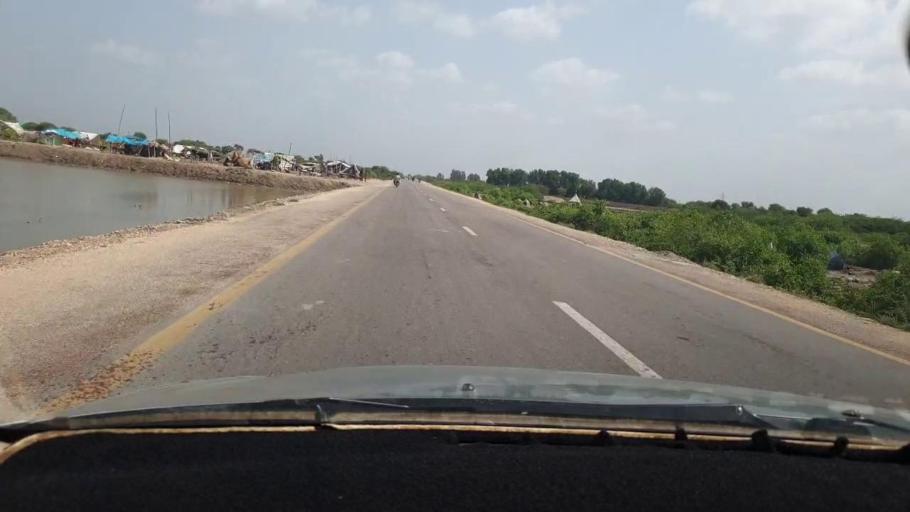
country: PK
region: Sindh
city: Digri
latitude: 25.1145
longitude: 69.1572
